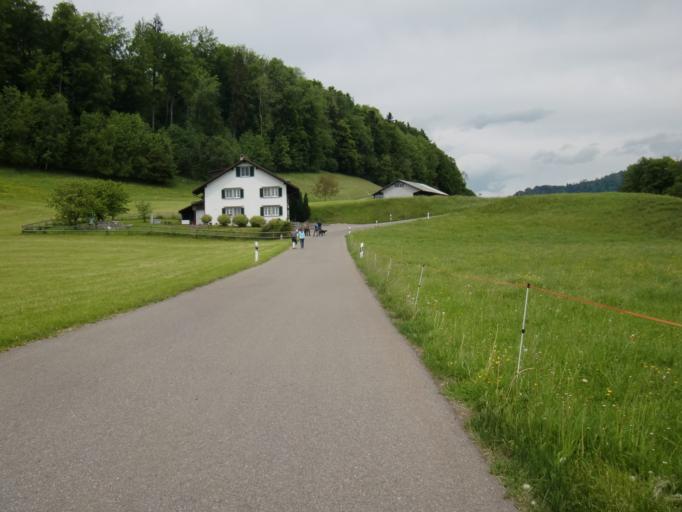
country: CH
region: Zurich
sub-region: Bezirk Hinwil
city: Wald
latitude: 47.2801
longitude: 8.9041
